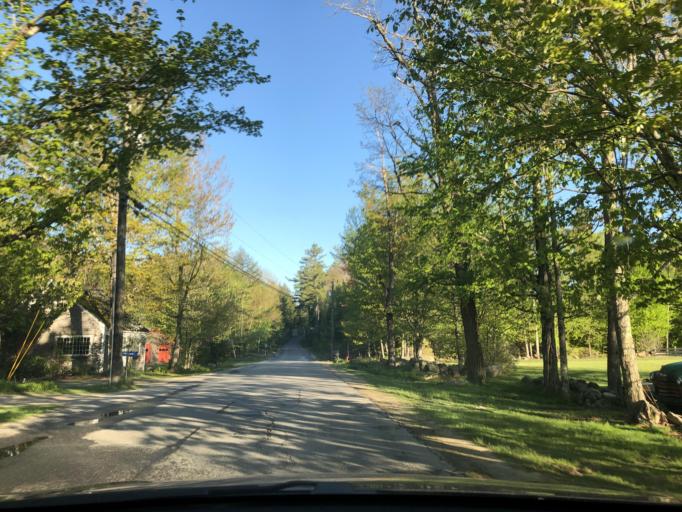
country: US
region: New Hampshire
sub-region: Merrimack County
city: New London
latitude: 43.4078
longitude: -71.9926
